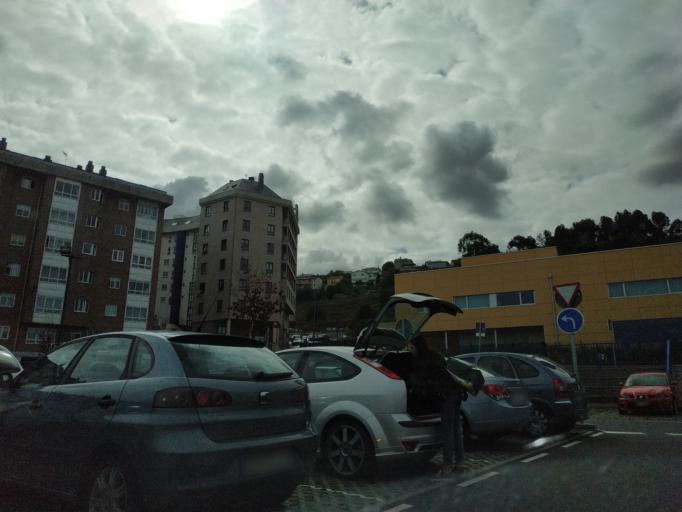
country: ES
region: Galicia
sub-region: Provincia da Coruna
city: Culleredo
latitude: 43.3263
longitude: -8.3841
